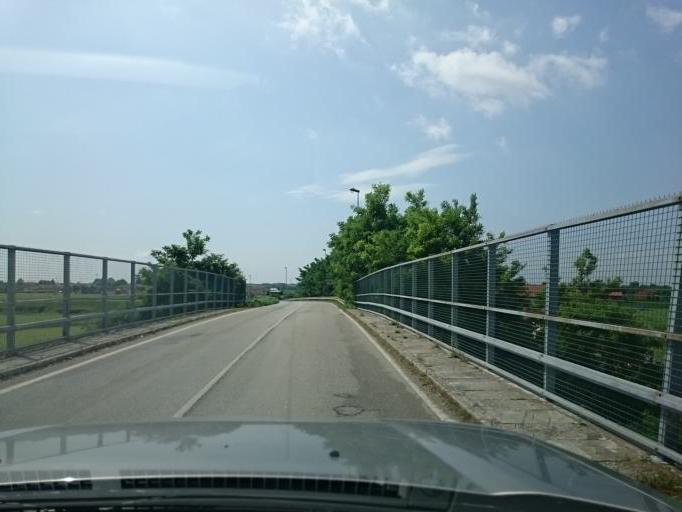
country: IT
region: Veneto
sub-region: Provincia di Padova
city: Masera di Padova
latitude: 45.3393
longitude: 11.8521
